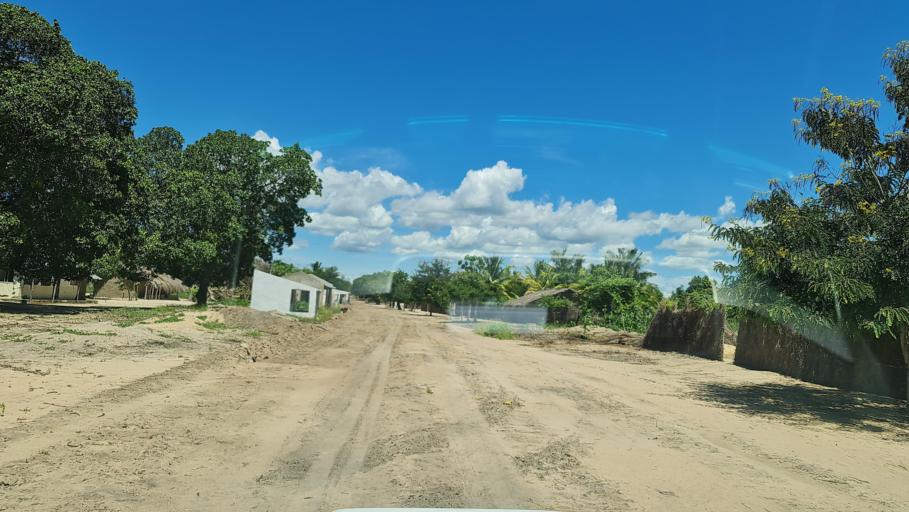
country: MZ
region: Nampula
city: Nampula
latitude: -15.2998
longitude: 39.8684
